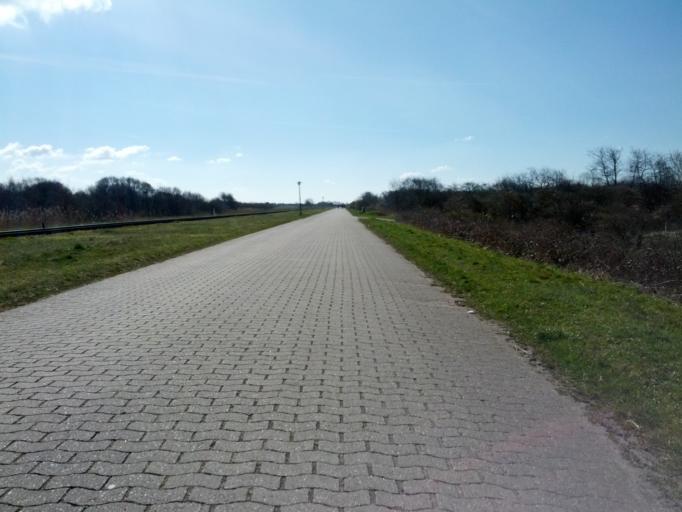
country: DE
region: Lower Saxony
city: Langeoog
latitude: 53.7409
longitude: 7.4896
